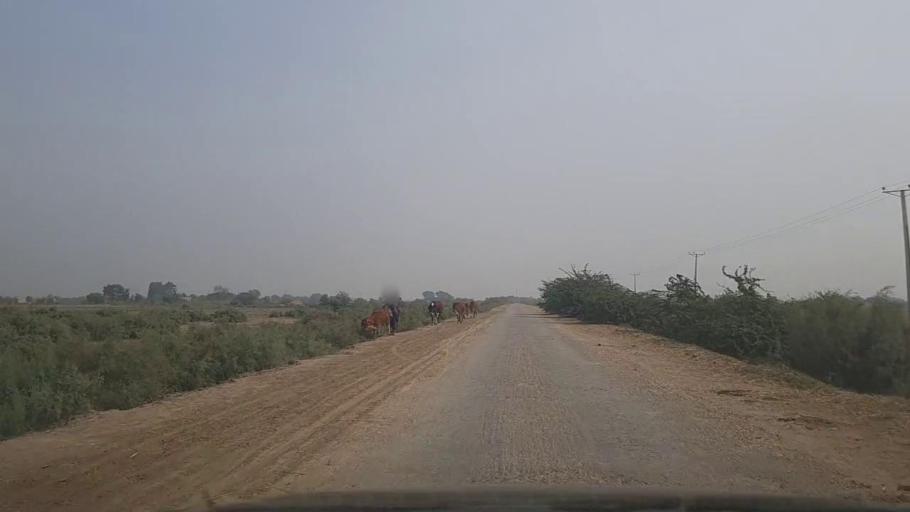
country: PK
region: Sindh
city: Mirpur Sakro
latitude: 24.4790
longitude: 67.6539
